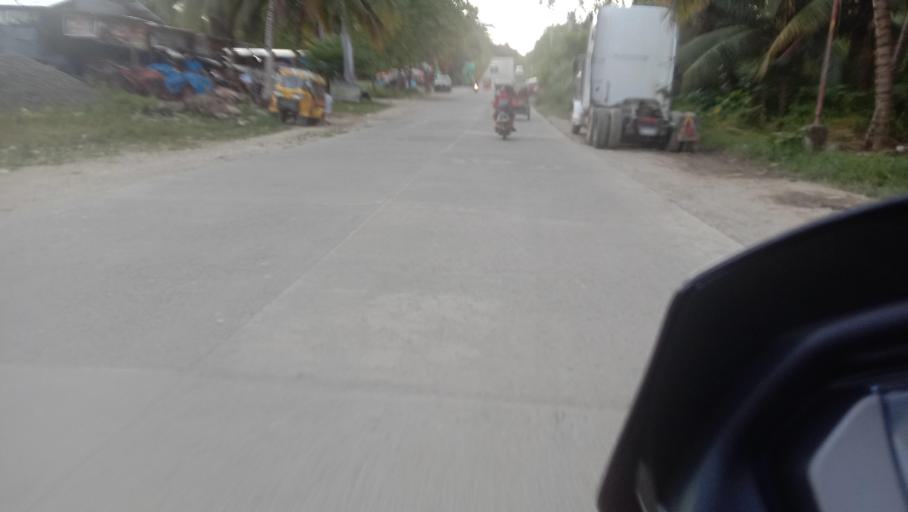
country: PH
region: Caraga
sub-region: Province of Surigao del Sur
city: Barobo
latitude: 8.5313
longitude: 126.1196
